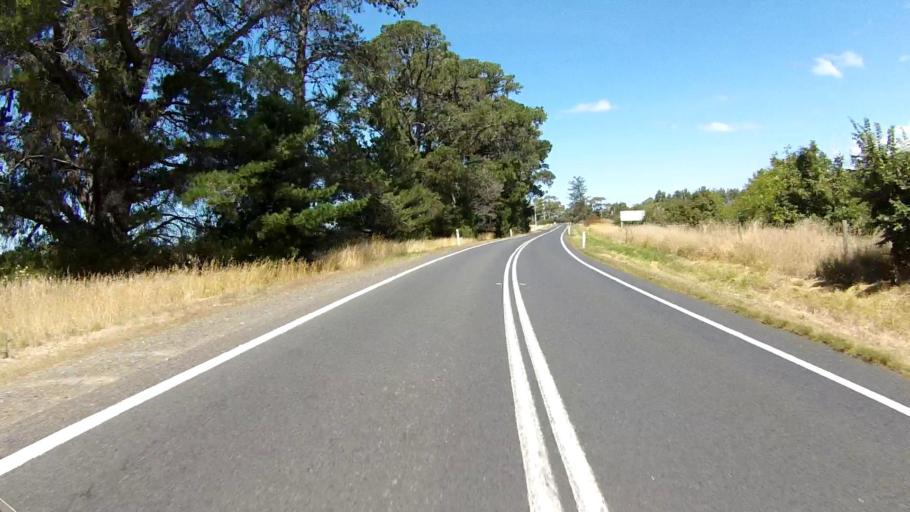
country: AU
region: Tasmania
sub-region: Break O'Day
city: St Helens
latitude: -42.0649
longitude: 148.0637
